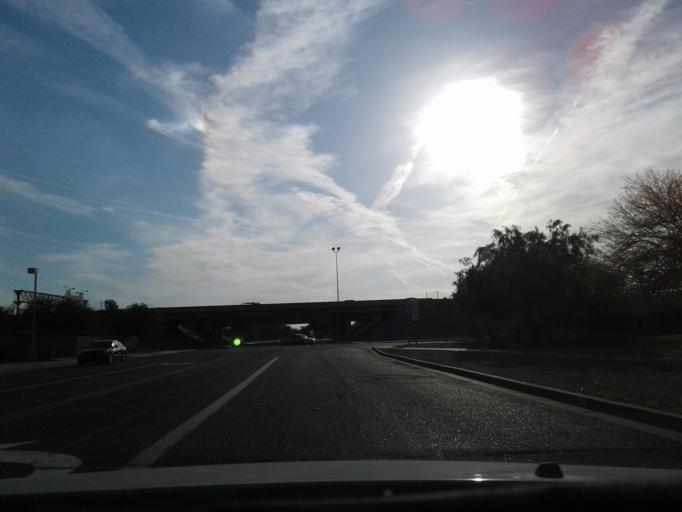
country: US
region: Arizona
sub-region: Maricopa County
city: Phoenix
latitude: 33.4413
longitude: -112.0356
